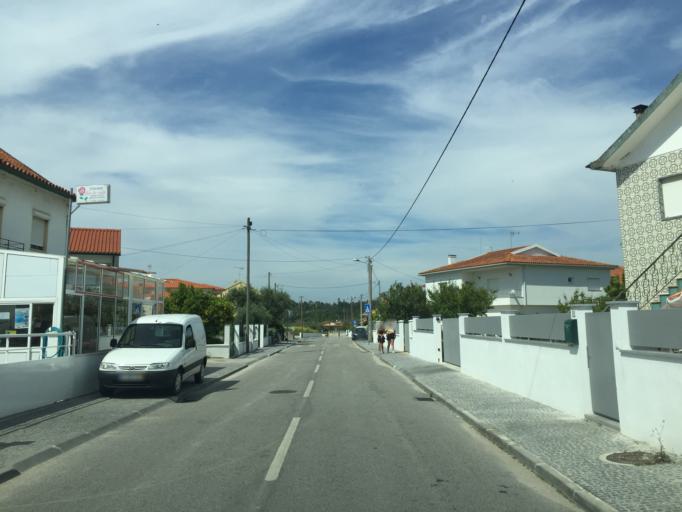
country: PT
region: Coimbra
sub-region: Soure
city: Soure
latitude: 40.0066
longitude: -8.5807
